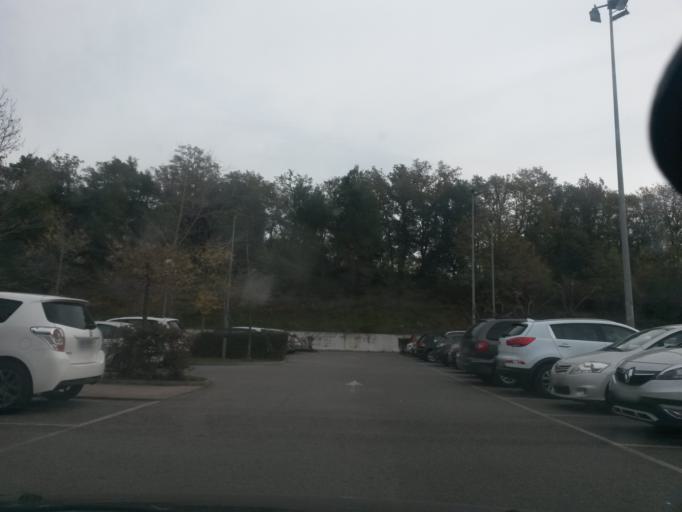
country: ES
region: Catalonia
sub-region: Provincia de Girona
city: Salt
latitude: 41.9586
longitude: 2.8123
